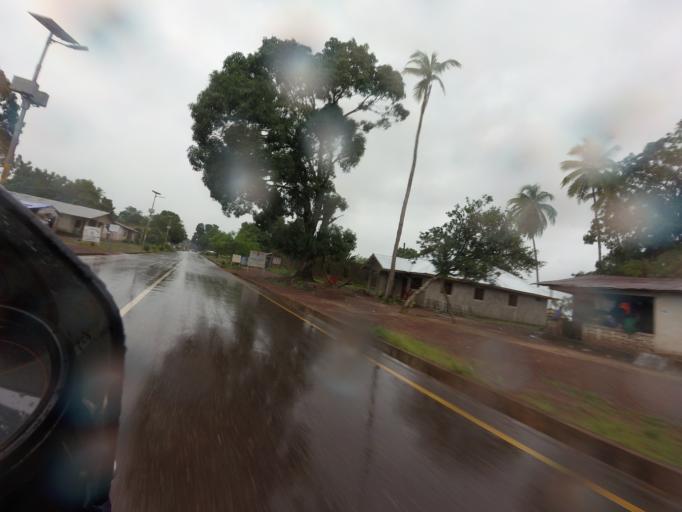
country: SL
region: Northern Province
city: Kambia
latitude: 9.1243
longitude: -12.9152
